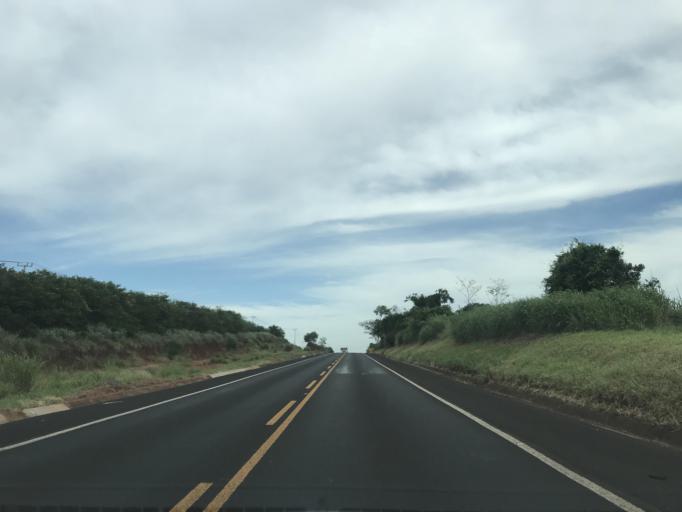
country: BR
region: Parana
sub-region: Paranavai
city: Paranavai
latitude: -23.0166
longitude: -52.5081
